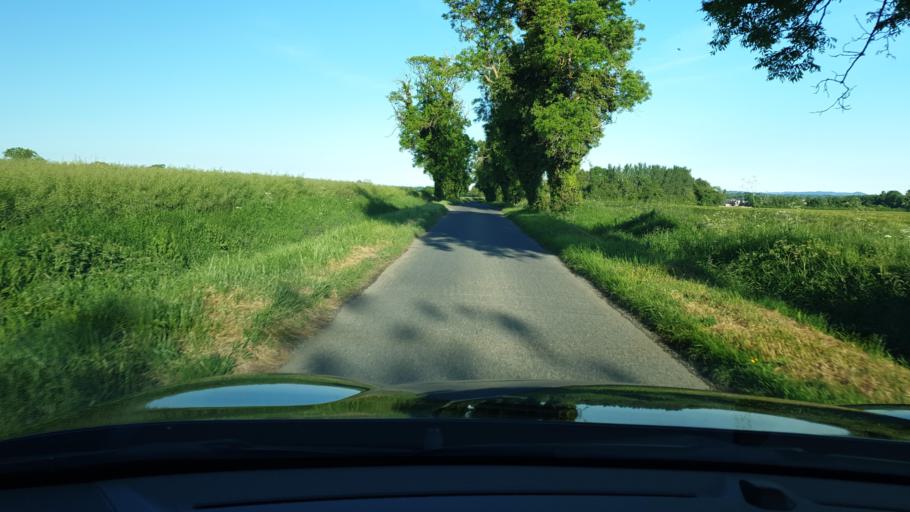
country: IE
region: Leinster
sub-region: Fingal County
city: Swords
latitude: 53.5025
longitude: -6.2379
